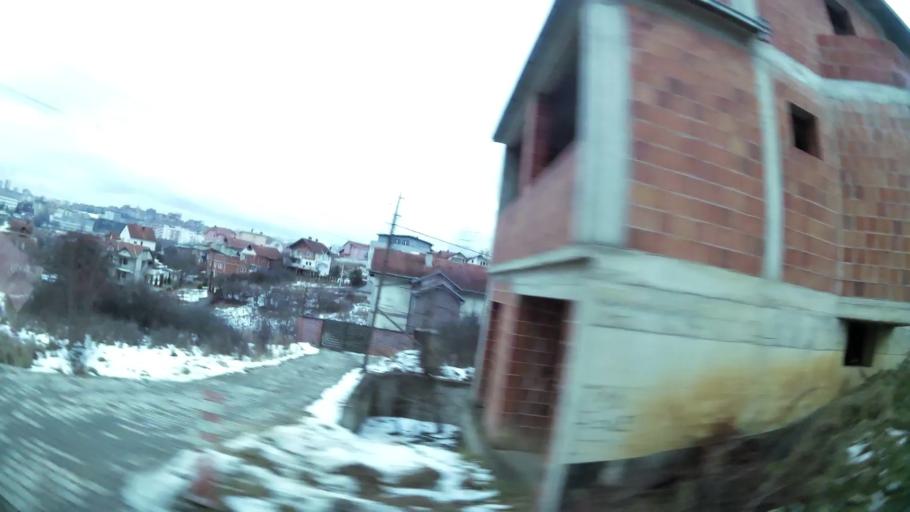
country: XK
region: Pristina
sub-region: Komuna e Prishtines
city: Pristina
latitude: 42.6384
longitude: 21.1642
